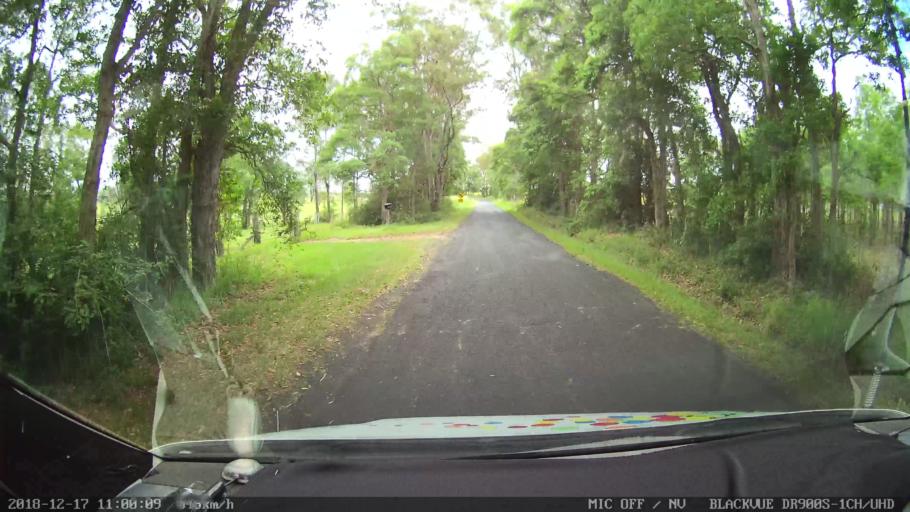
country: AU
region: New South Wales
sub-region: Richmond Valley
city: Casino
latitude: -28.8193
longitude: 152.6173
